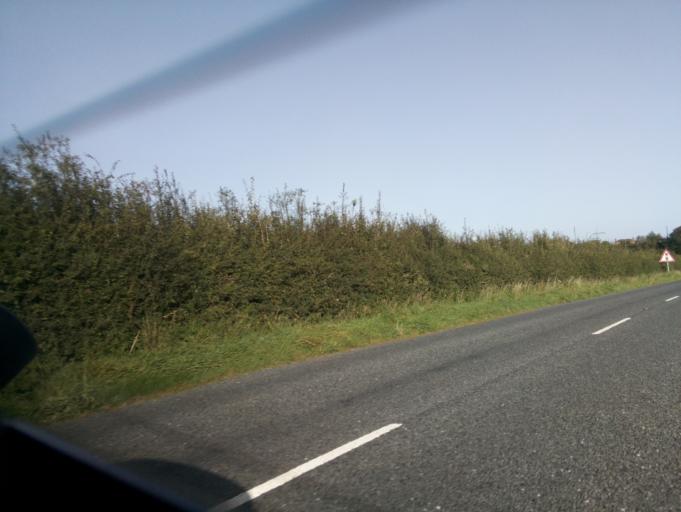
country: GB
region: England
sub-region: Gloucestershire
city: Tewkesbury
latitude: 51.9580
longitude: -2.1623
